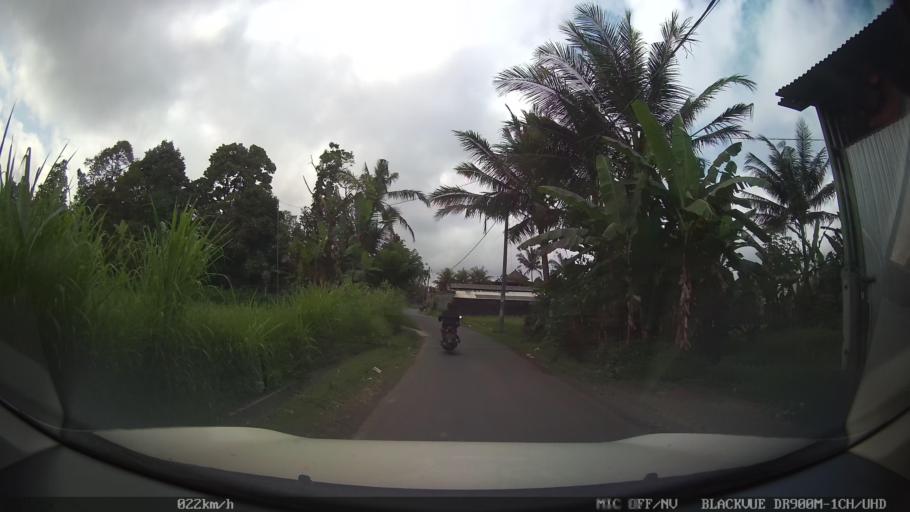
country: ID
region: Bali
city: Banjar Petak
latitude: -8.4420
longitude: 115.3227
